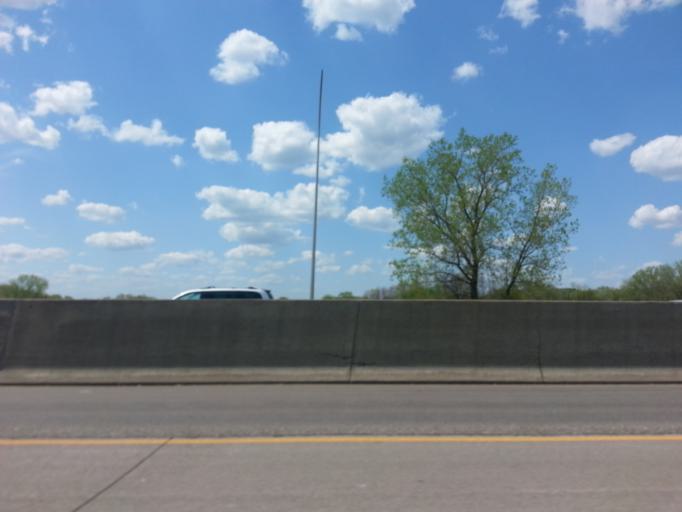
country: US
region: Minnesota
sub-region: Washington County
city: Newport
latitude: 44.8992
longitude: -92.9956
